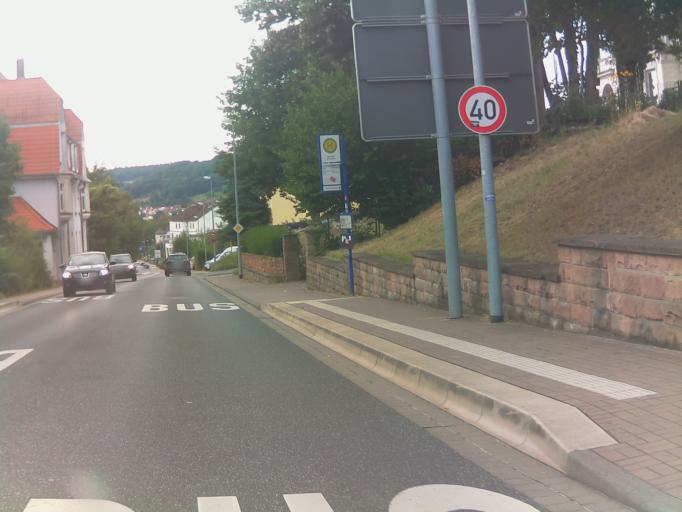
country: DE
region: Hesse
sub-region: Regierungsbezirk Darmstadt
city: Bad Orb
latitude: 50.2212
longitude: 9.3550
